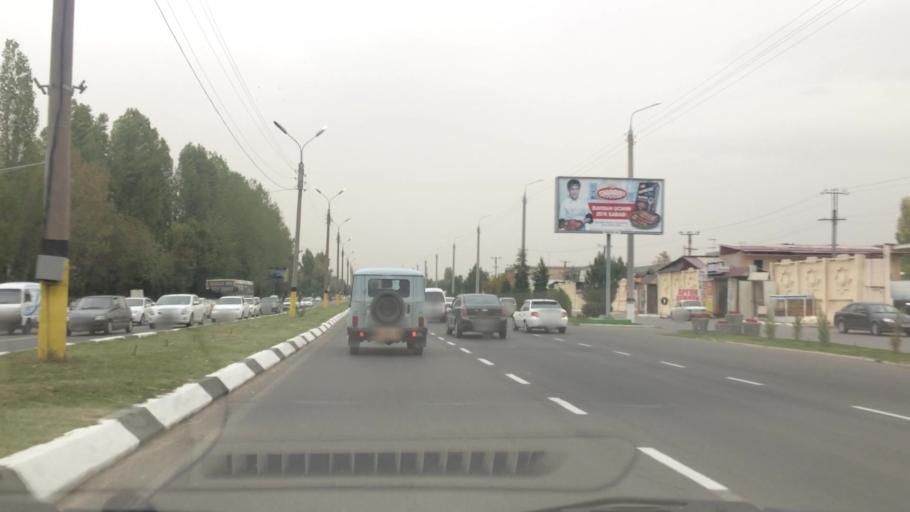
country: UZ
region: Toshkent
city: Salor
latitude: 41.3164
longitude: 69.3556
